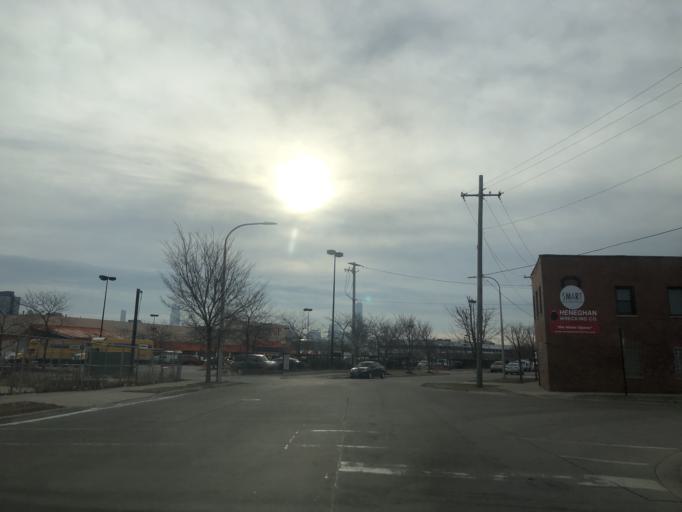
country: US
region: Illinois
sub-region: Cook County
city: Chicago
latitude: 41.9129
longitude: -87.6607
